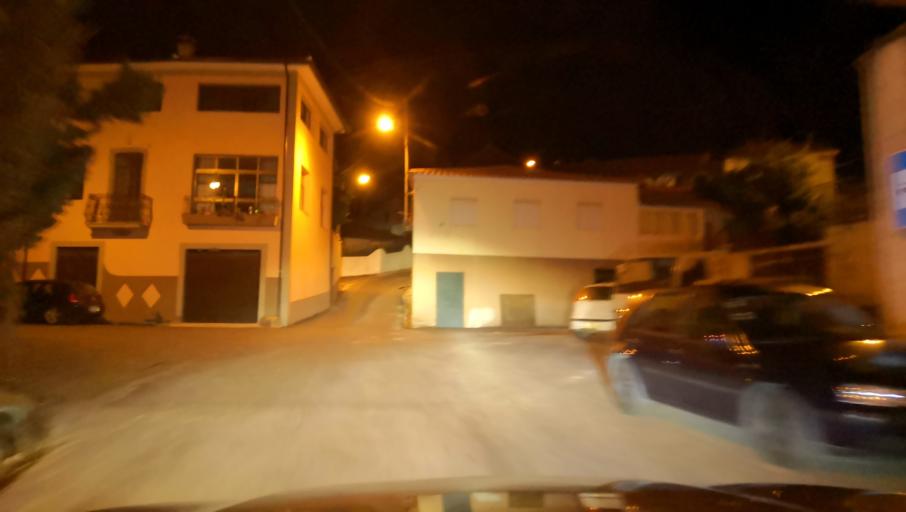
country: PT
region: Vila Real
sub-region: Sabrosa
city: Vilela
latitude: 41.2084
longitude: -7.6941
